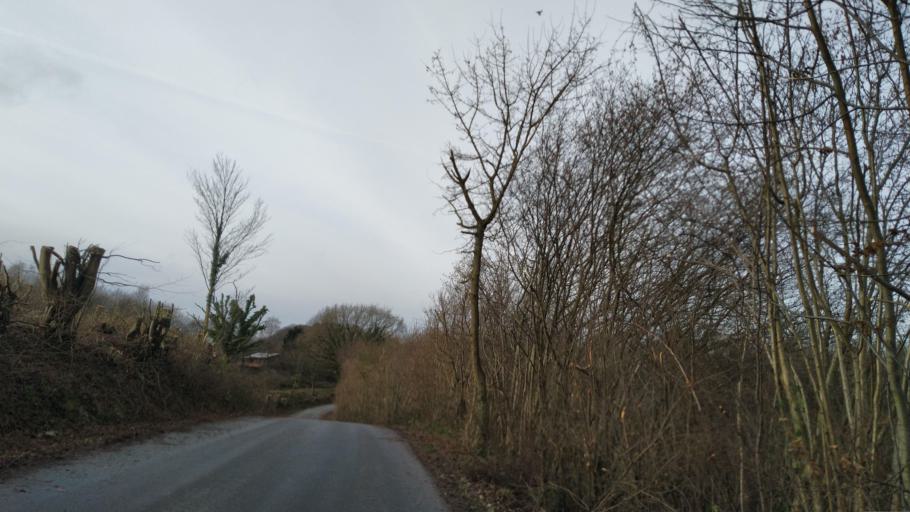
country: DE
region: Schleswig-Holstein
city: Malente
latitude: 54.1975
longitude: 10.6018
